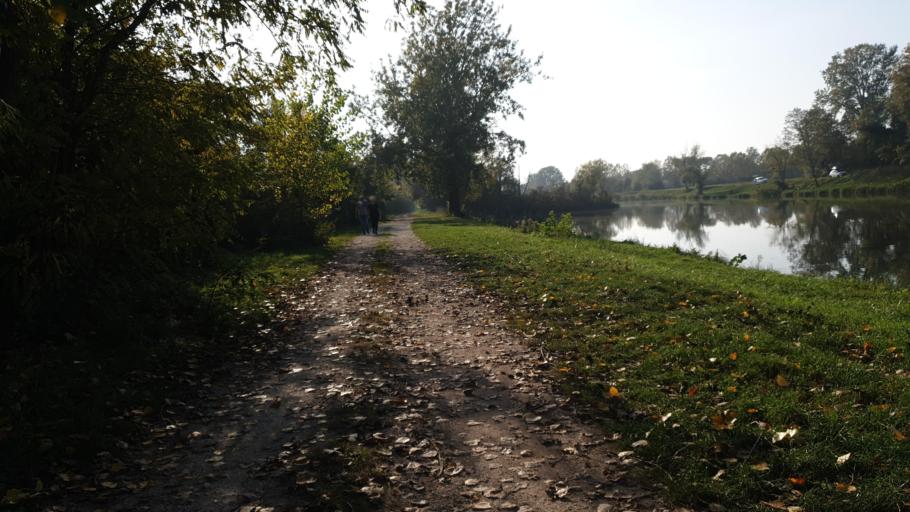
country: IT
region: Veneto
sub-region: Provincia di Venezia
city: Vigonovo
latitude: 45.3890
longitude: 11.9937
